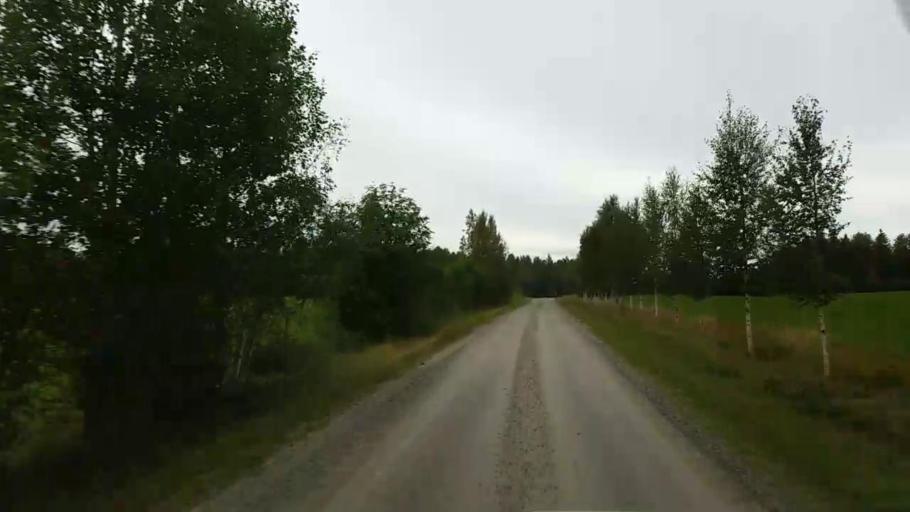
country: SE
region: Gaevleborg
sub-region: Ljusdals Kommun
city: Farila
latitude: 61.8086
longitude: 15.8622
